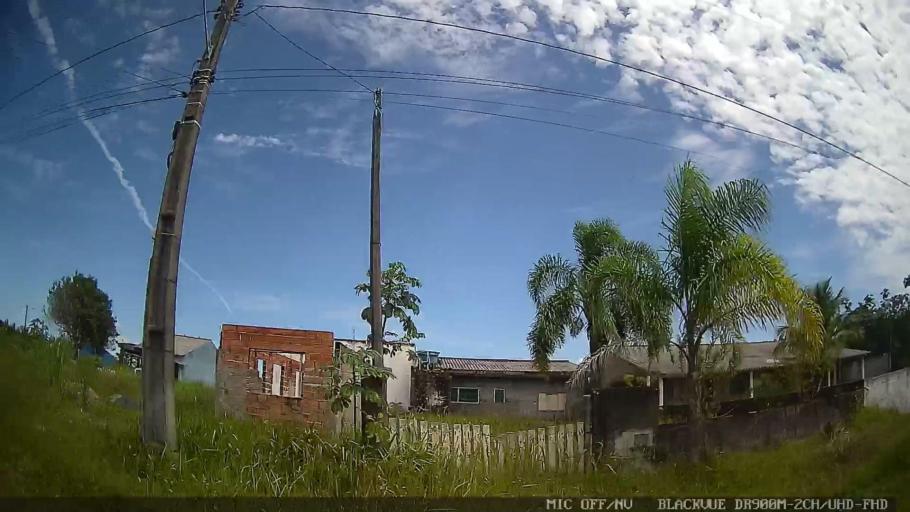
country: BR
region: Sao Paulo
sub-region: Iguape
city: Iguape
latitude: -24.7241
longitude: -47.5202
